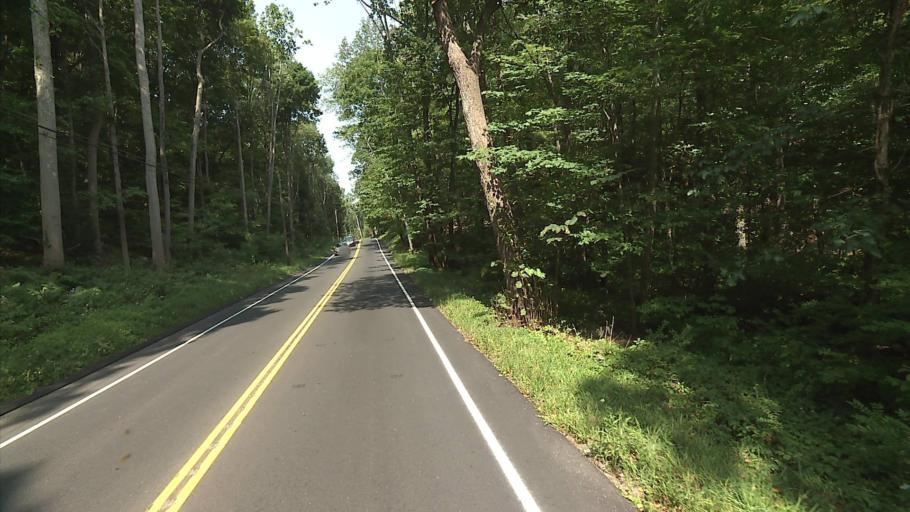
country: US
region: Connecticut
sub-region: Fairfield County
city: Bethel
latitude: 41.3487
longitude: -73.3811
